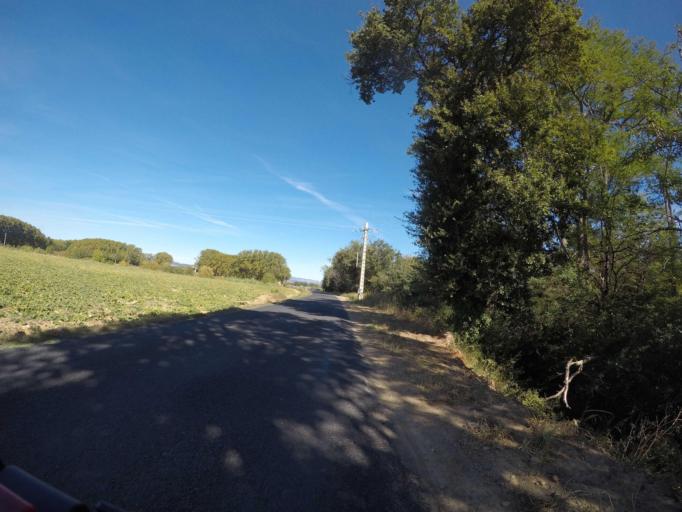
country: FR
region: Languedoc-Roussillon
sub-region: Departement des Pyrenees-Orientales
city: Le Soler
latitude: 42.6600
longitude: 2.7966
